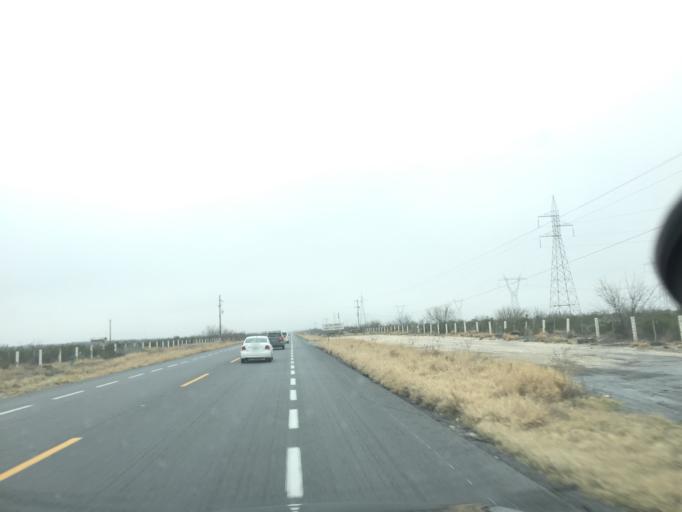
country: MX
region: Nuevo Leon
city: Bustamante
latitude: 26.4453
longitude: -101.0167
